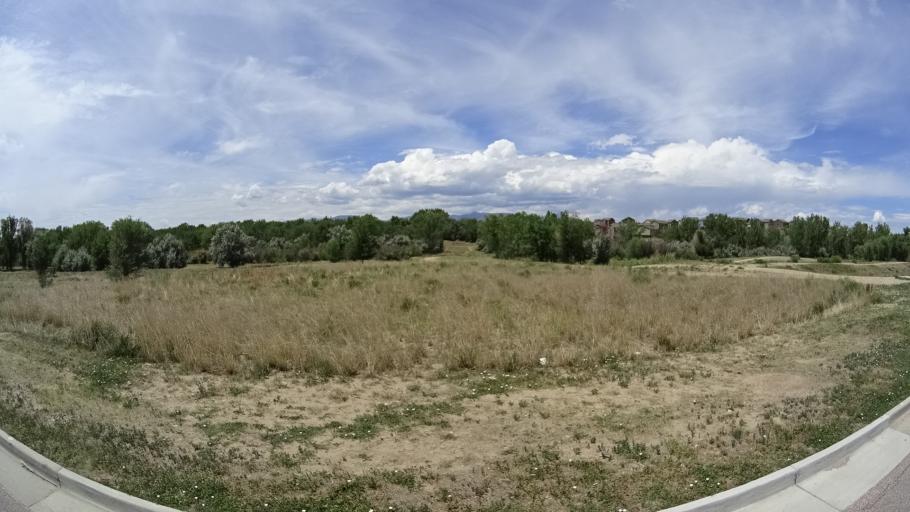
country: US
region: Colorado
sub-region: El Paso County
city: Fountain
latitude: 38.6901
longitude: -104.6850
